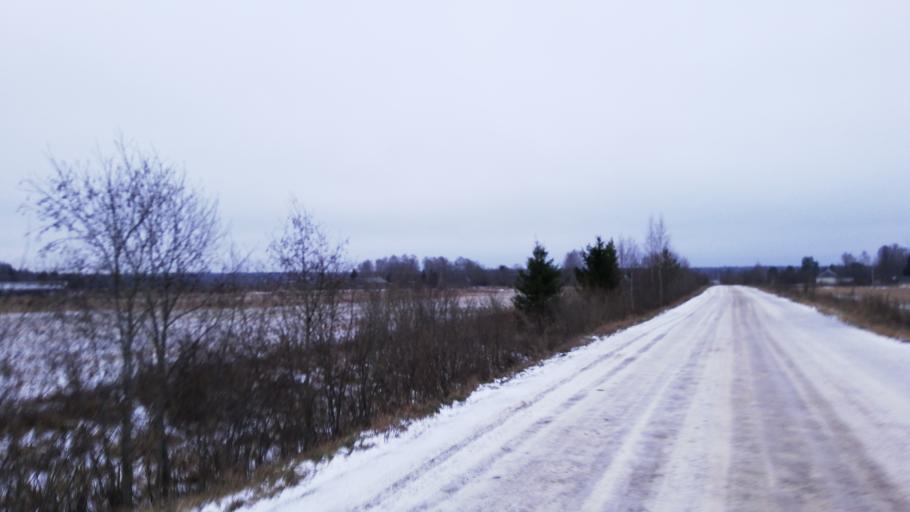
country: RU
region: Kostroma
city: Krasnoye-na-Volge
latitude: 57.6750
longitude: 41.1952
